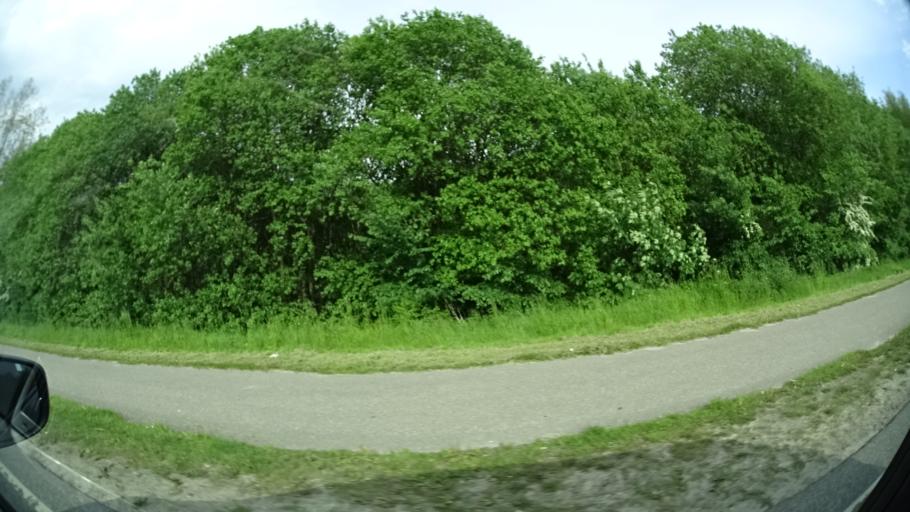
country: DK
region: Central Jutland
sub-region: Arhus Kommune
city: Beder
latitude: 56.0969
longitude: 10.2096
